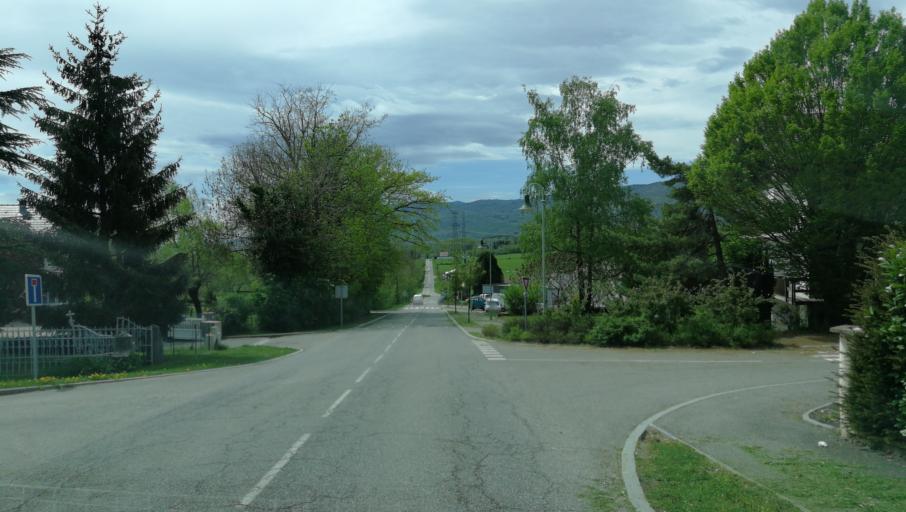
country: FR
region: Rhone-Alpes
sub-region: Departement de l'Ain
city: Bellegarde-sur-Valserine
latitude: 46.0750
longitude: 5.7836
